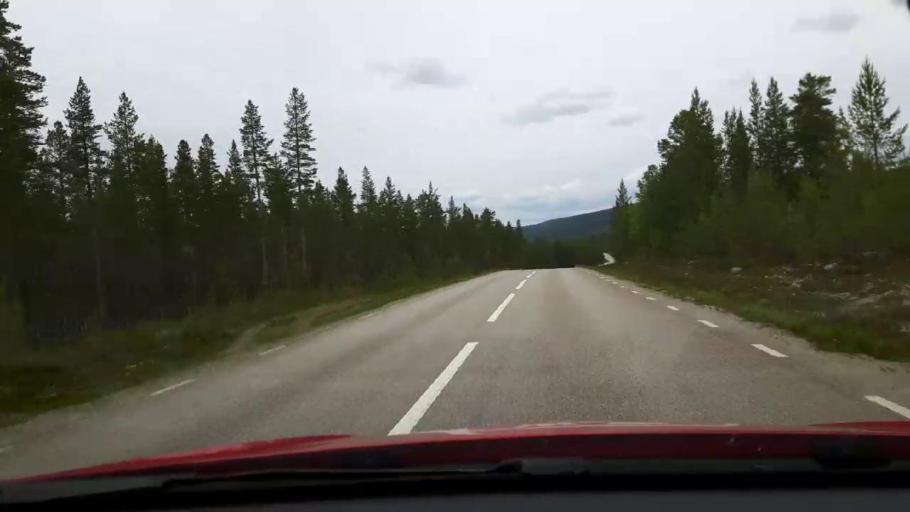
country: SE
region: Jaemtland
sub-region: Harjedalens Kommun
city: Sveg
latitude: 62.2554
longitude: 13.8403
